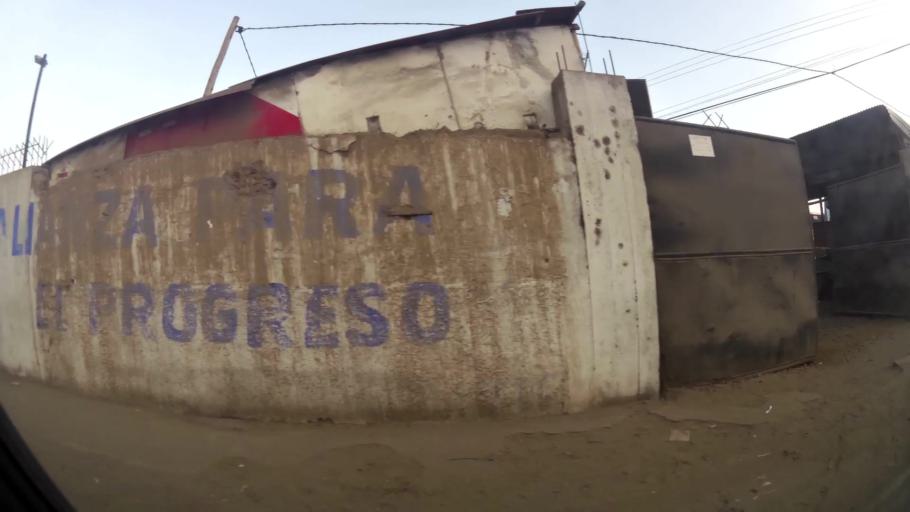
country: PE
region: La Libertad
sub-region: Provincia de Trujillo
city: La Esperanza
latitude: -8.0968
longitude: -79.0389
